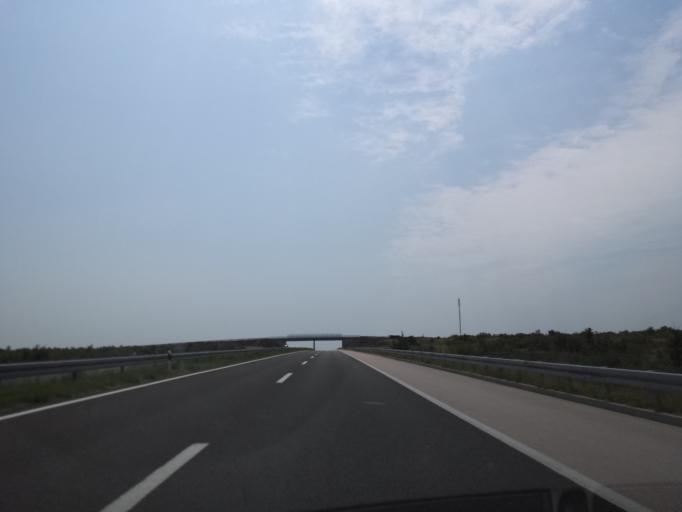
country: HR
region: Zadarska
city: Policnik
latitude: 44.1447
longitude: 15.4205
